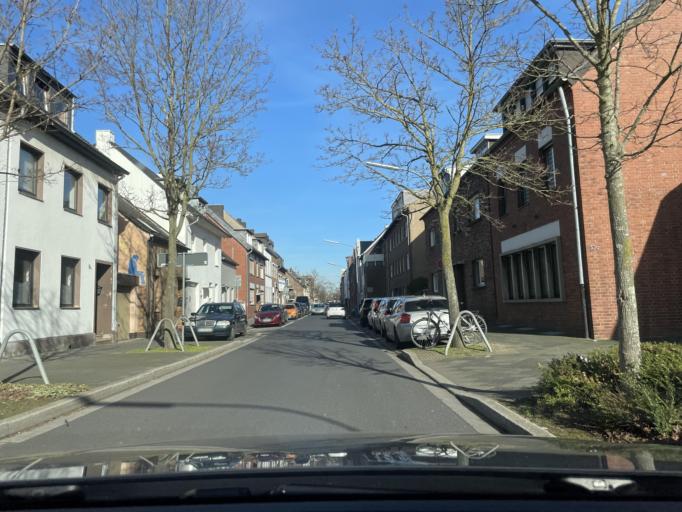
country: DE
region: North Rhine-Westphalia
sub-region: Regierungsbezirk Dusseldorf
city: Neuss
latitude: 51.2135
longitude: 6.6618
